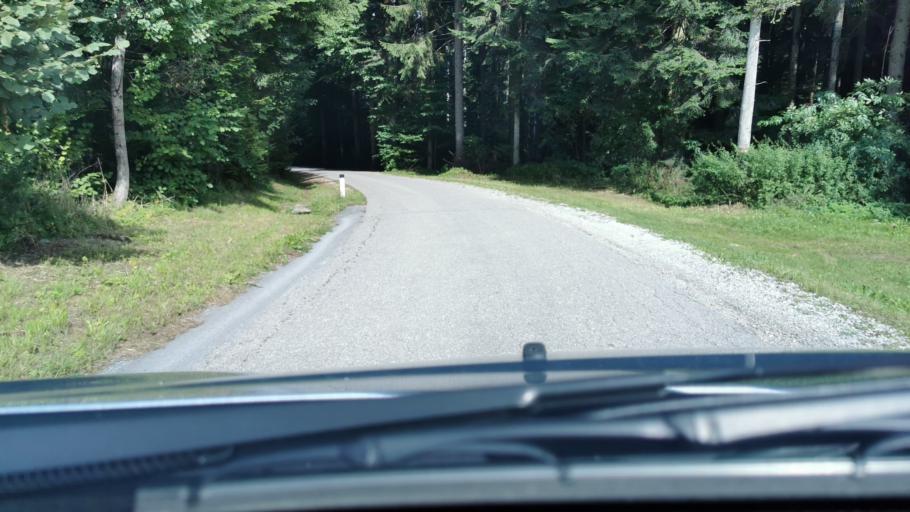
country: AT
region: Styria
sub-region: Politischer Bezirk Weiz
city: Gschaid bei Birkfeld
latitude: 47.3290
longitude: 15.7098
